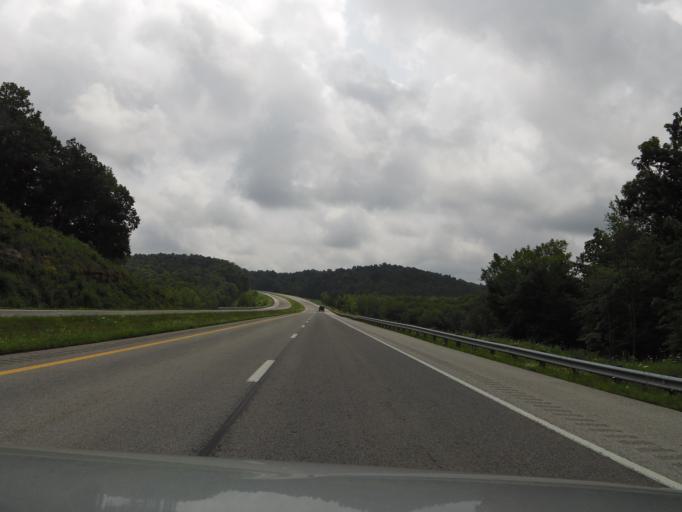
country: US
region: Kentucky
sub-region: Ohio County
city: Oak Grove
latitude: 37.3889
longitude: -86.7002
